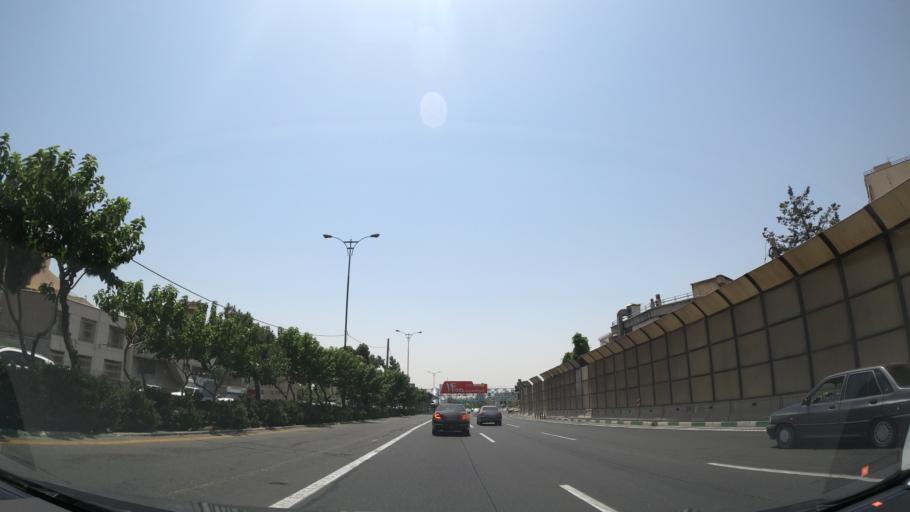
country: IR
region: Tehran
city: Tehran
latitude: 35.7264
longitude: 51.3822
